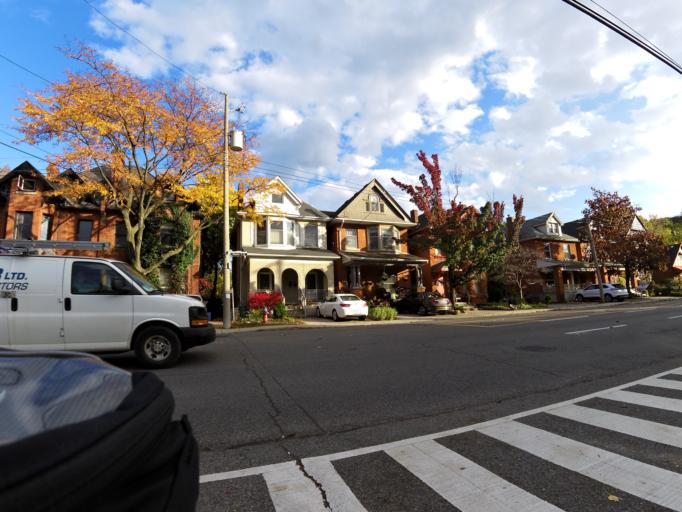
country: CA
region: Ontario
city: Hamilton
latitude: 43.2497
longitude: -79.8828
